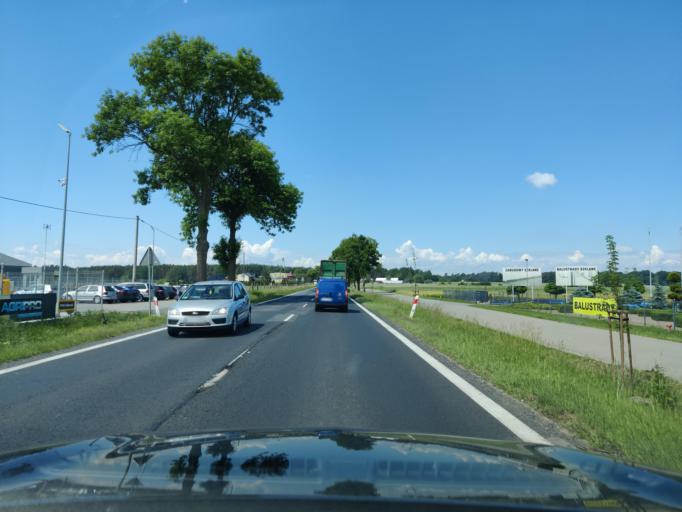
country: PL
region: Greater Poland Voivodeship
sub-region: Powiat grodziski
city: Rakoniewice
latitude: 52.1335
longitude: 16.2570
